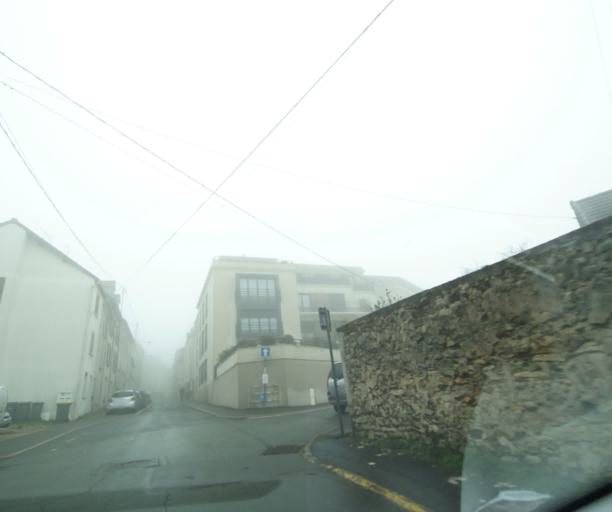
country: FR
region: Ile-de-France
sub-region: Departement de Seine-et-Marne
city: Dammartin-en-Goele
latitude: 49.0532
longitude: 2.6792
